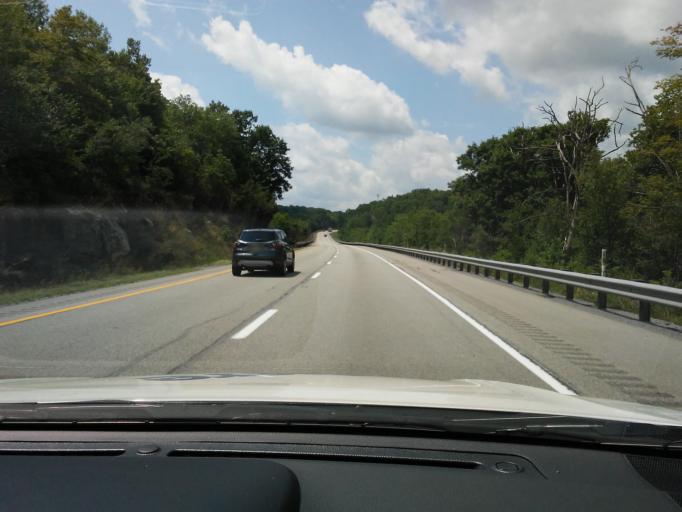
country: US
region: Pennsylvania
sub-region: Clearfield County
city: Troy
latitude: 40.9664
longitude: -78.0913
